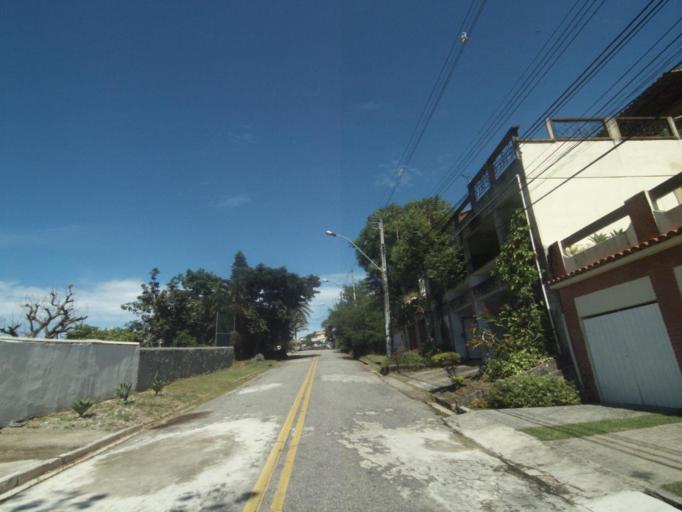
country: BR
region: Rio de Janeiro
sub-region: Niteroi
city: Niteroi
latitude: -22.9535
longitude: -43.0625
